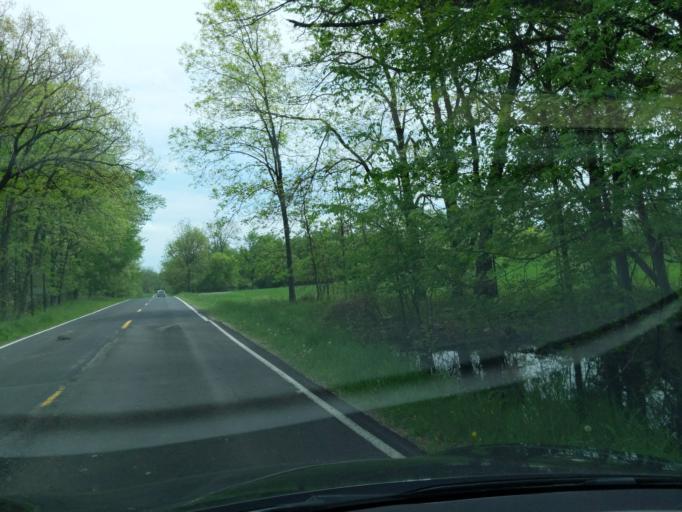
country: US
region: Michigan
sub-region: Ingham County
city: Stockbridge
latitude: 42.4685
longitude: -84.1755
